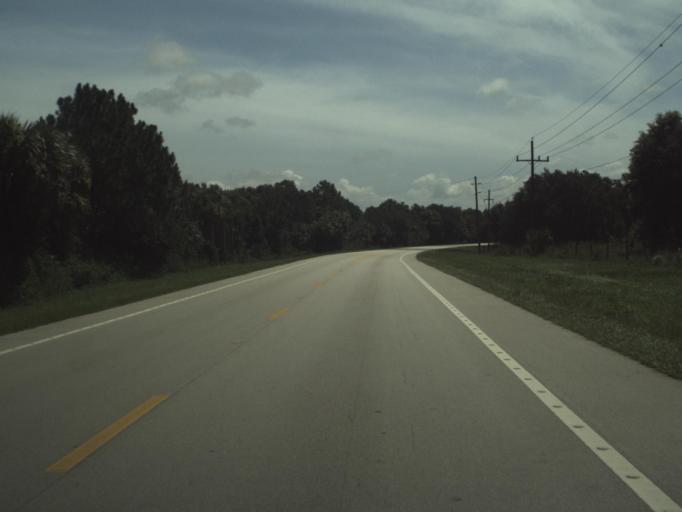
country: US
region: Florida
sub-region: Martin County
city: Indiantown
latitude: 27.0126
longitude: -80.5481
